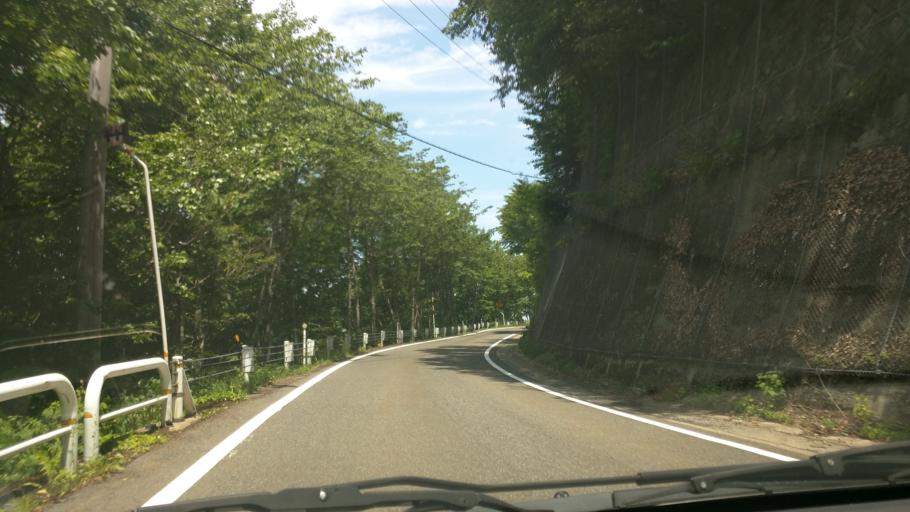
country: JP
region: Fukushima
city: Kitakata
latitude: 37.3393
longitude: 139.8733
